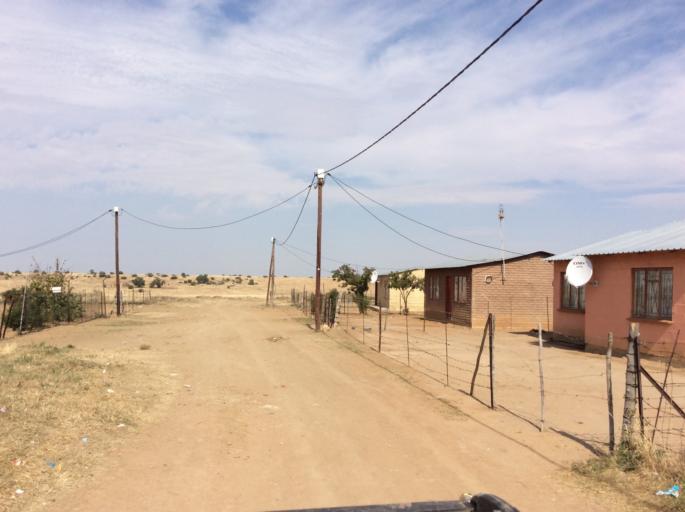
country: ZA
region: Orange Free State
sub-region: Xhariep District Municipality
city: Dewetsdorp
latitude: -29.5954
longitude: 26.6832
